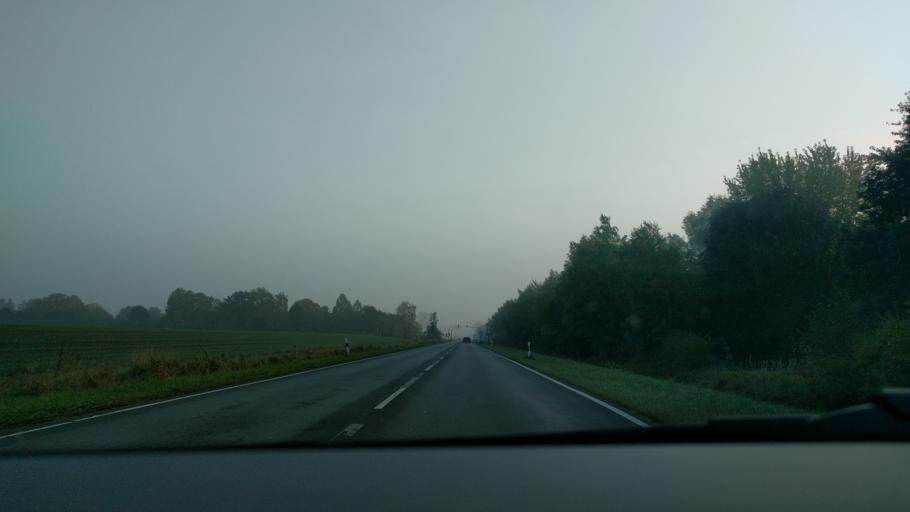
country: DE
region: Lower Saxony
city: Calberlah
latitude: 52.4322
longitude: 10.6604
